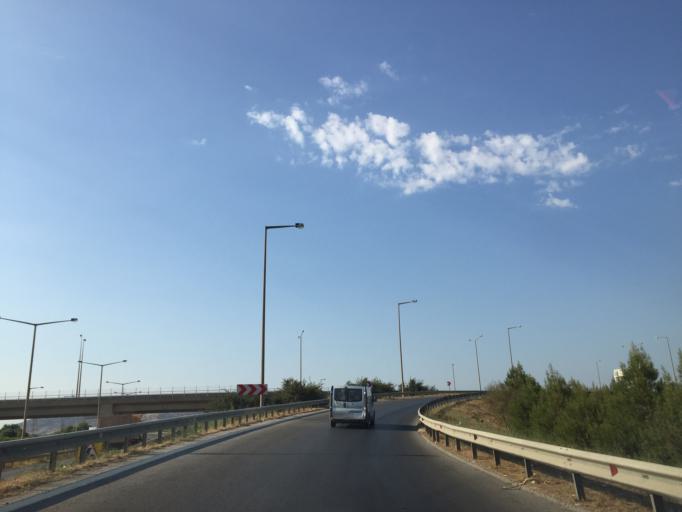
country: TR
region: Izmir
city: Belevi
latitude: 38.0302
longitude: 27.4442
